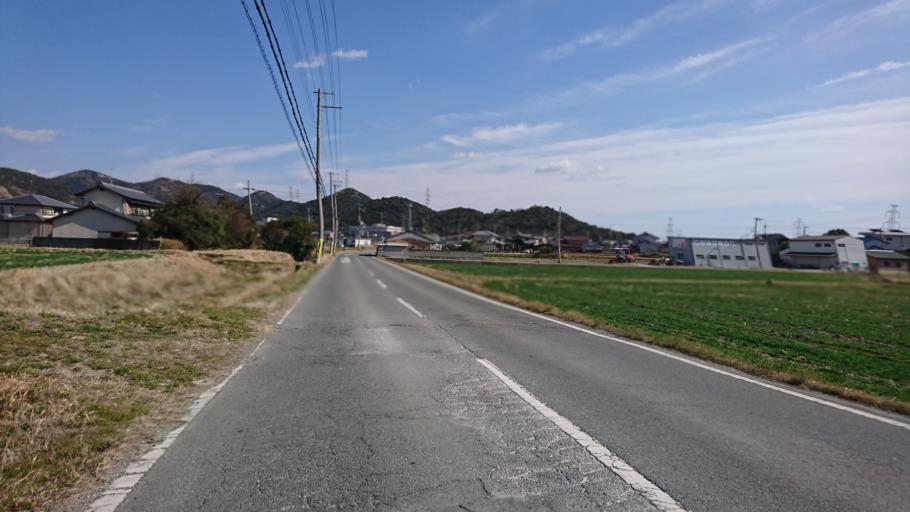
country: JP
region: Hyogo
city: Kakogawacho-honmachi
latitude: 34.8040
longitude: 134.8260
